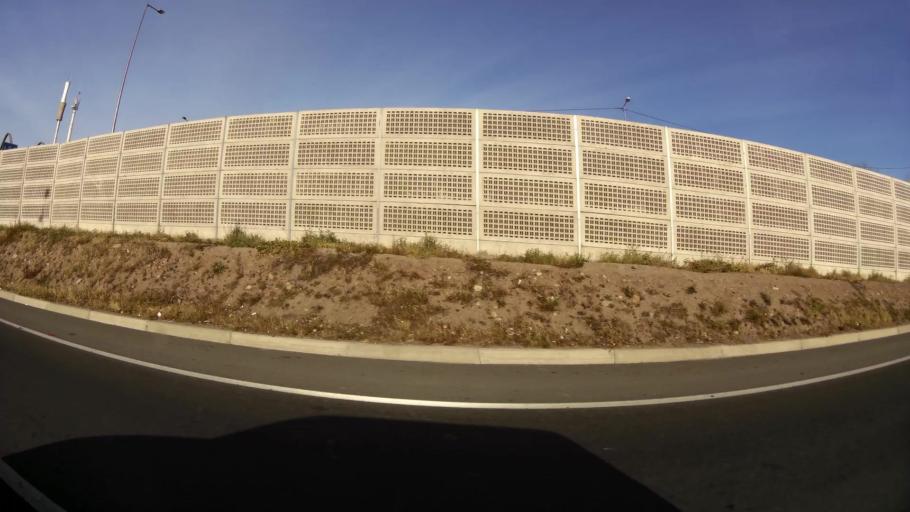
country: CL
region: Santiago Metropolitan
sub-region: Provincia de Santiago
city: La Pintana
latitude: -33.5818
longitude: -70.6111
